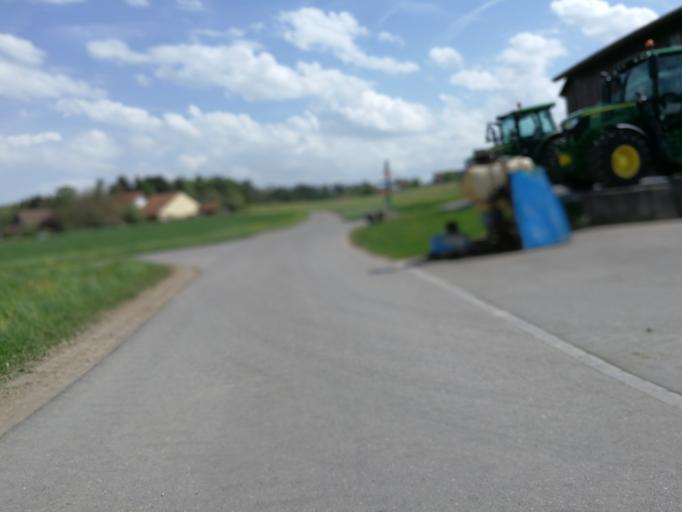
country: CH
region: Zurich
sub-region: Bezirk Meilen
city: Oetwil am See
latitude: 47.2834
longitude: 8.7322
